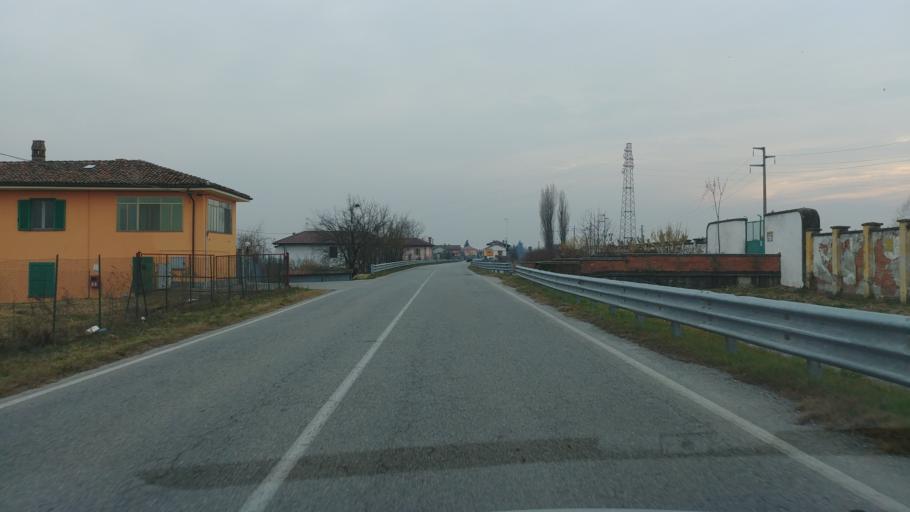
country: IT
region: Piedmont
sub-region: Provincia di Cuneo
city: Fossano
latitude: 44.5282
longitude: 7.7066
